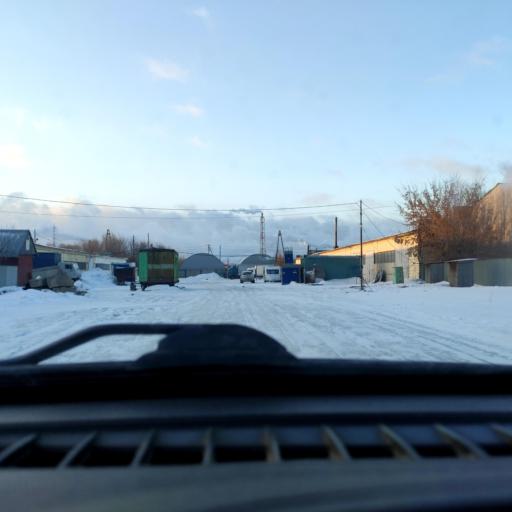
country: RU
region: Samara
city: Tol'yatti
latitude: 53.5649
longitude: 49.4846
